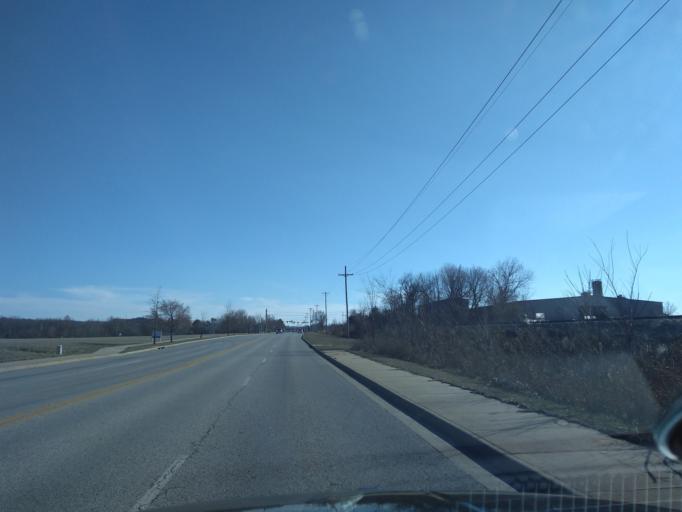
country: US
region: Arkansas
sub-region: Washington County
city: Johnson
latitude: 36.1202
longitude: -94.1635
